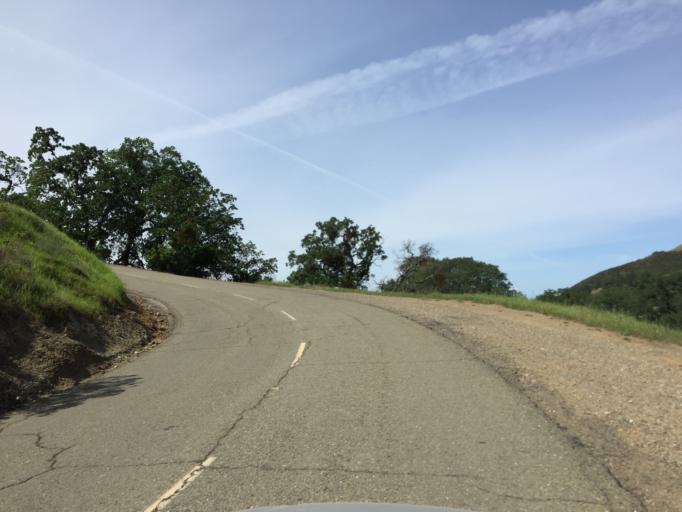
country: US
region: California
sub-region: Contra Costa County
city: Diablo
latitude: 37.8768
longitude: -121.9616
